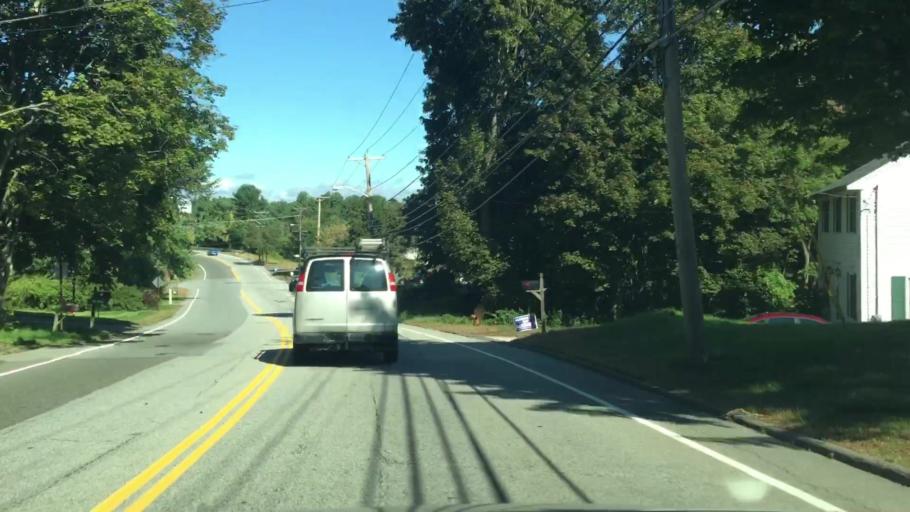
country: US
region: Massachusetts
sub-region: Essex County
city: Haverhill
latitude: 42.8017
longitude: -71.0828
